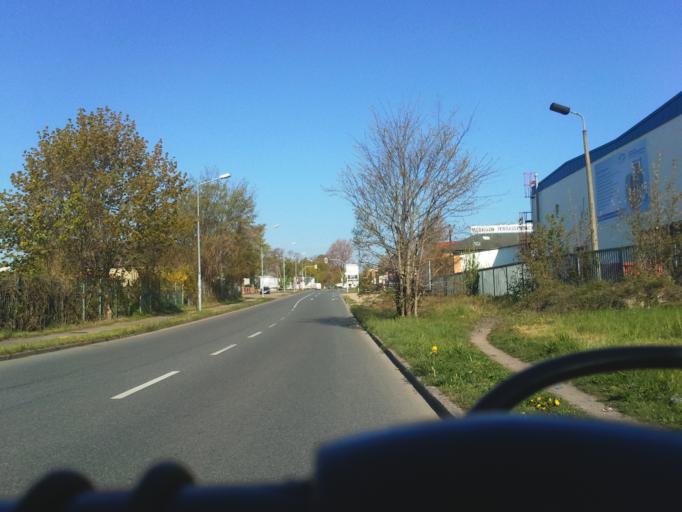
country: DE
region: Mecklenburg-Vorpommern
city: Rostock
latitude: 54.0953
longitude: 12.1018
